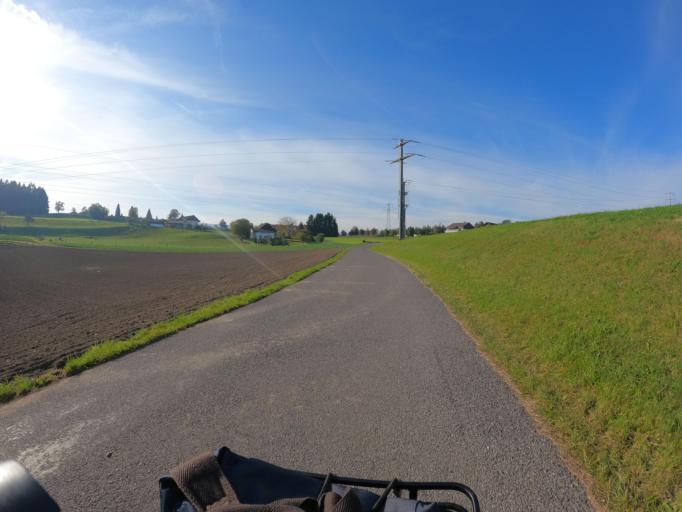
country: CH
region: Aargau
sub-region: Bezirk Muri
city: Aristau
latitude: 47.2758
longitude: 8.3577
